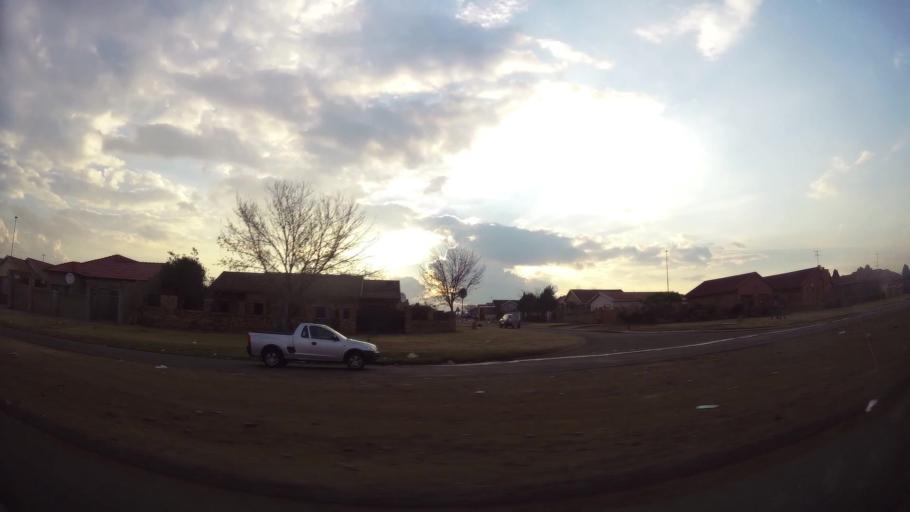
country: ZA
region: Gauteng
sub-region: City of Johannesburg Metropolitan Municipality
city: Orange Farm
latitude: -26.5891
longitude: 27.8519
